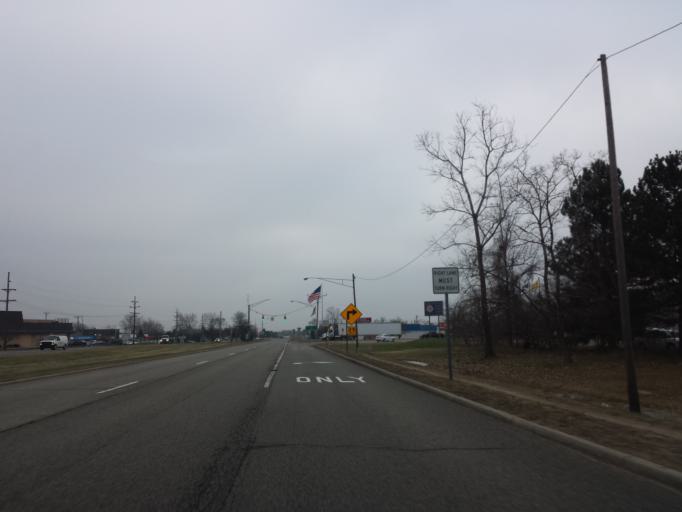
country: US
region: Michigan
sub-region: Oakland County
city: Clawson
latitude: 42.5570
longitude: -83.1289
